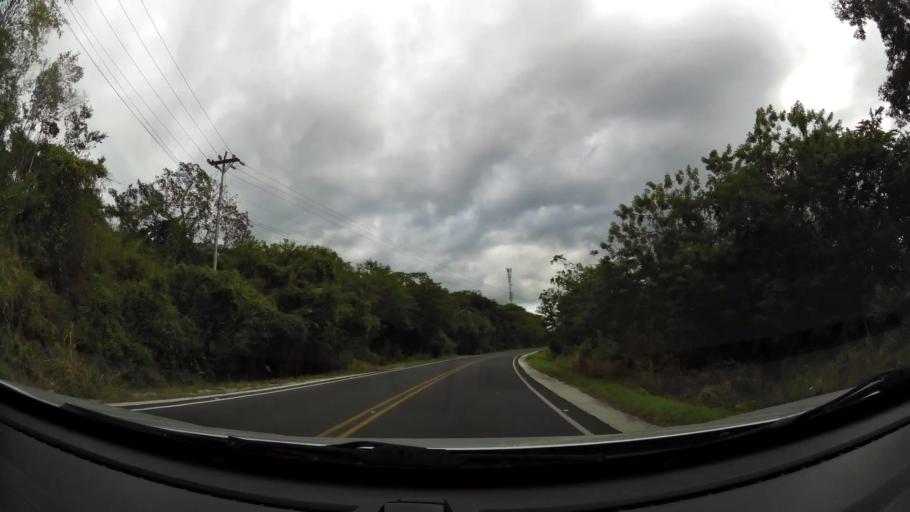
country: CR
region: Guanacaste
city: Nandayure
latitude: 10.2527
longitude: -85.2308
